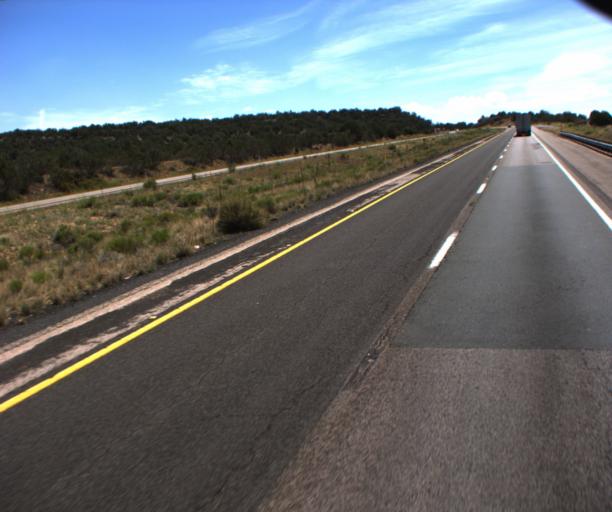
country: US
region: Arizona
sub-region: Mohave County
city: Peach Springs
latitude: 35.2864
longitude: -113.1041
